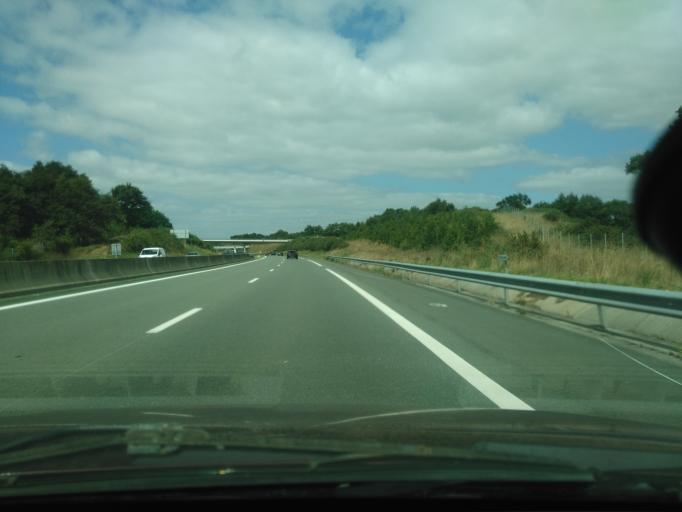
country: FR
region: Pays de la Loire
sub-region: Departement de la Vendee
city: Les Clouzeaux
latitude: 46.6421
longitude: -1.5049
